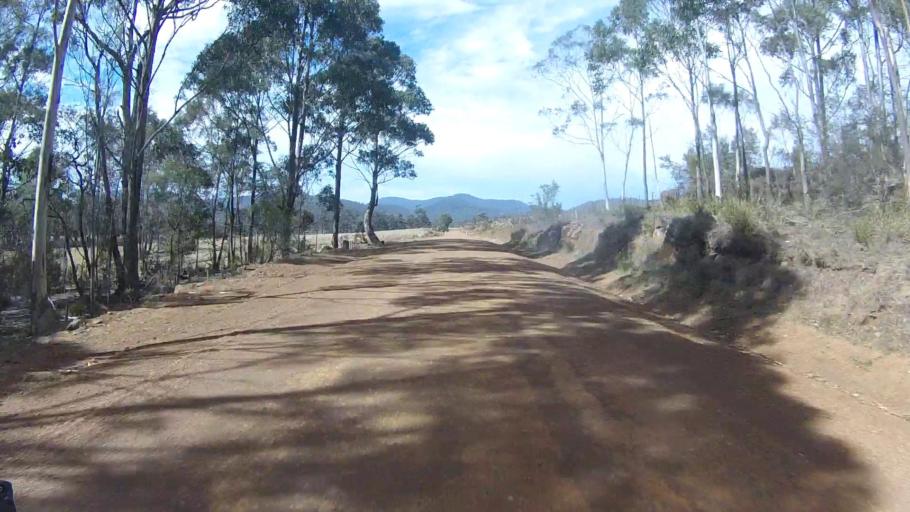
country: AU
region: Tasmania
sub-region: Sorell
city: Sorell
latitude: -42.6285
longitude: 147.9022
